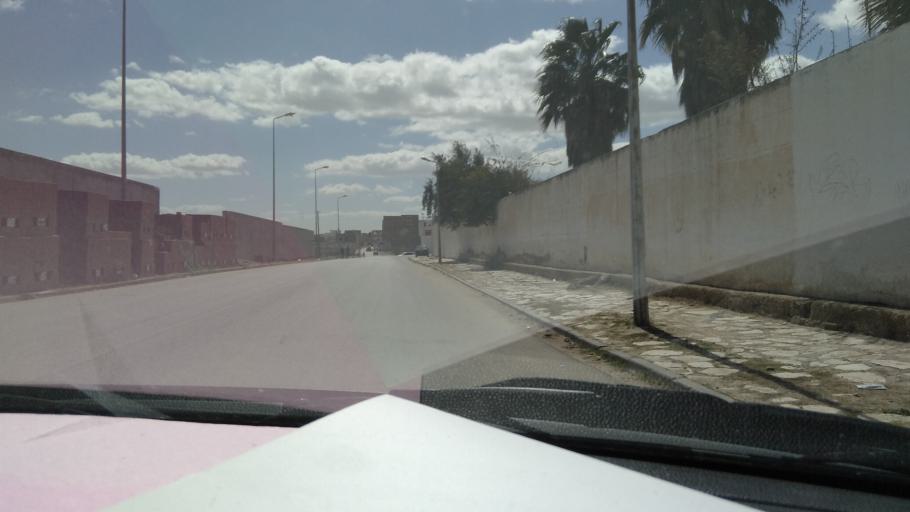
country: TN
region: Al Qayrawan
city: Kairouan
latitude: 35.6659
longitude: 10.1086
